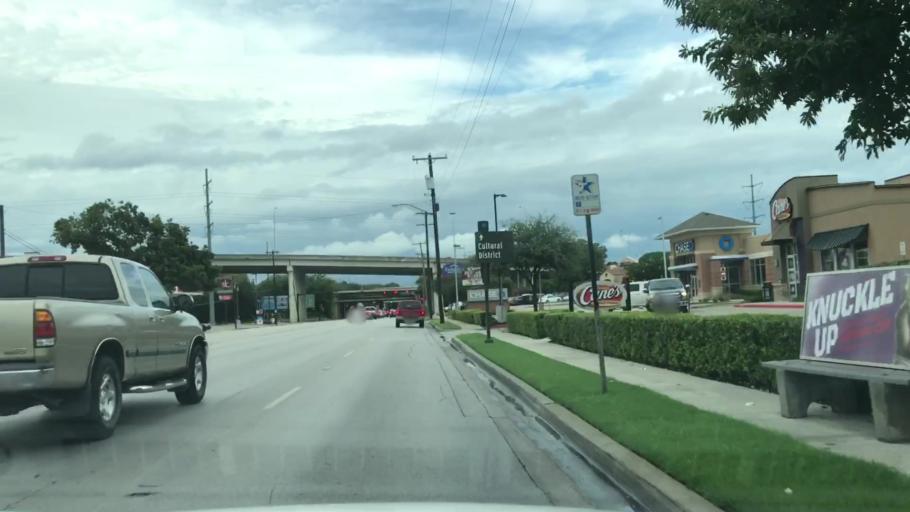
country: US
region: Texas
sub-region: Tarrant County
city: Fort Worth
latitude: 32.7289
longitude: -97.3612
